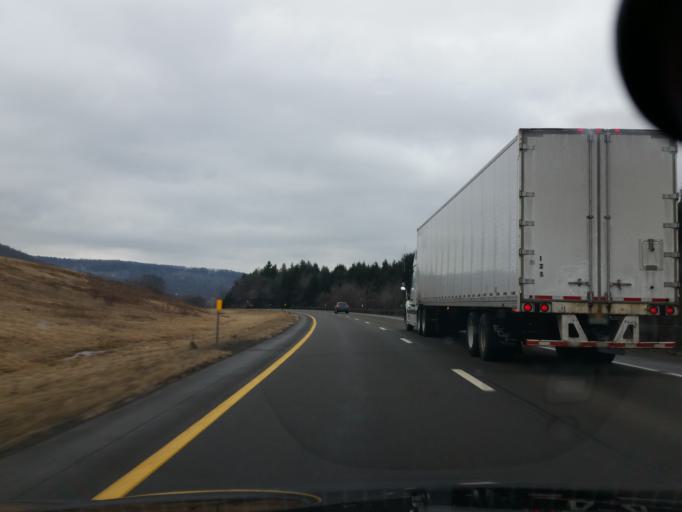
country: US
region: Pennsylvania
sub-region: Susquehanna County
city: Hallstead
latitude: 42.0196
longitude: -75.7823
